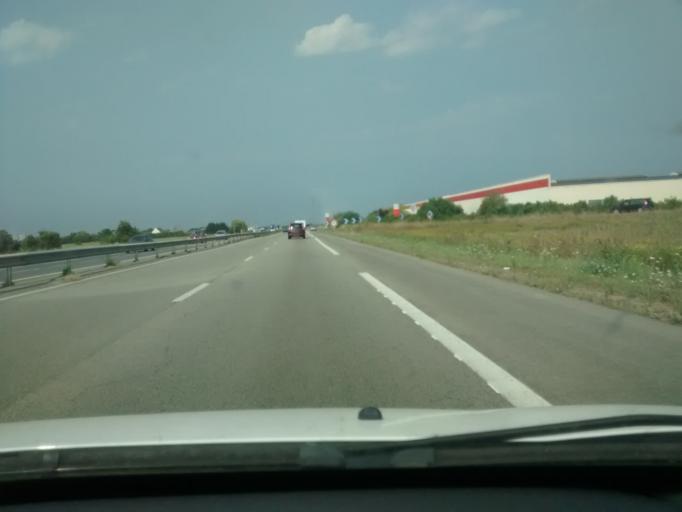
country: FR
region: Pays de la Loire
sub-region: Departement de la Loire-Atlantique
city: Montoir-de-Bretagne
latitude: 47.3245
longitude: -2.1653
